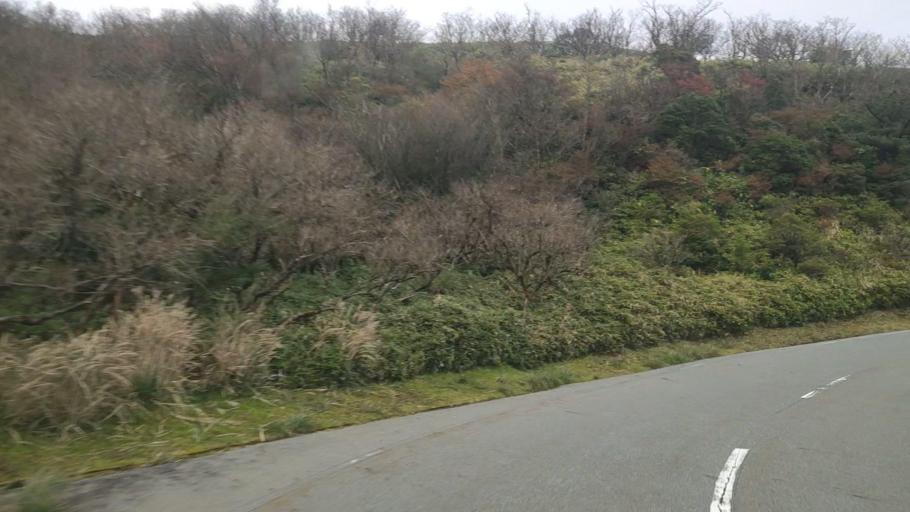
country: JP
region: Shizuoka
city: Heda
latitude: 34.9537
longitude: 138.8405
